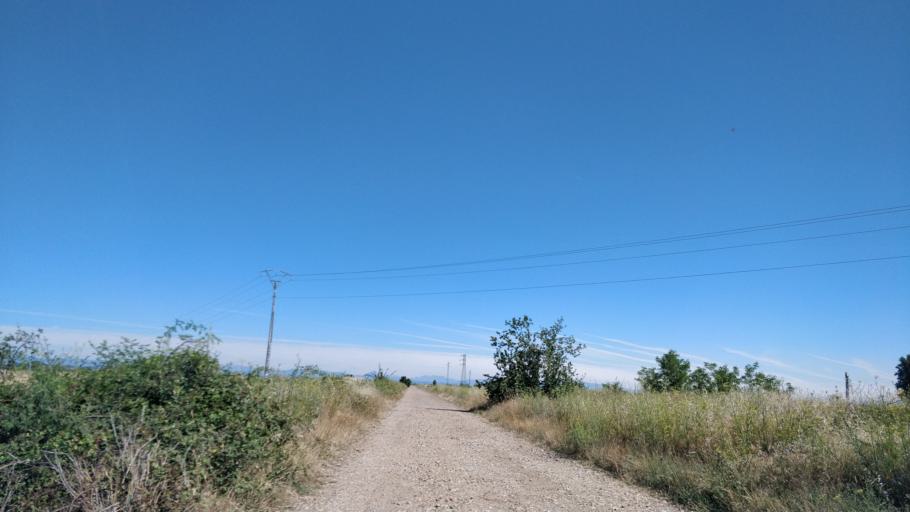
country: ES
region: Castille and Leon
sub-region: Provincia de Leon
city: Bustillo del Paramo
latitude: 42.4258
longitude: -5.8212
